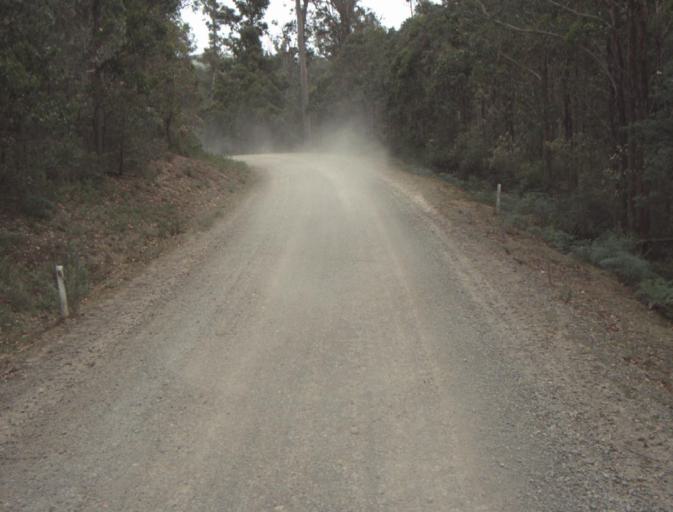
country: AU
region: Tasmania
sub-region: Dorset
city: Scottsdale
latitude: -41.3902
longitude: 147.5092
